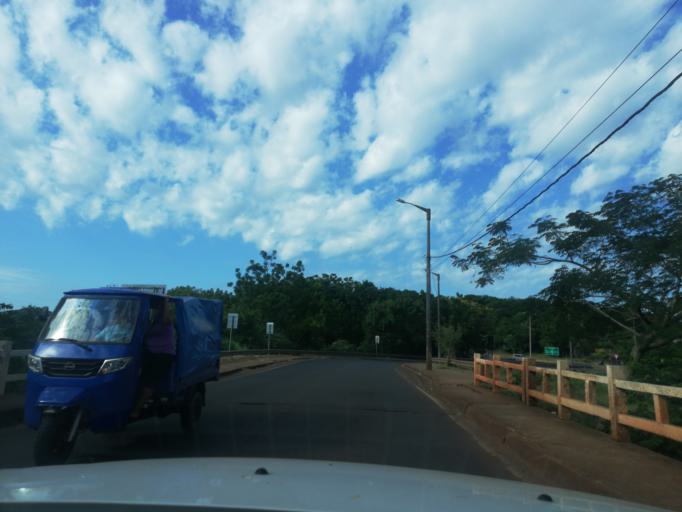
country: PY
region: Itapua
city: Encarnacion
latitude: -27.3430
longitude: -55.8524
